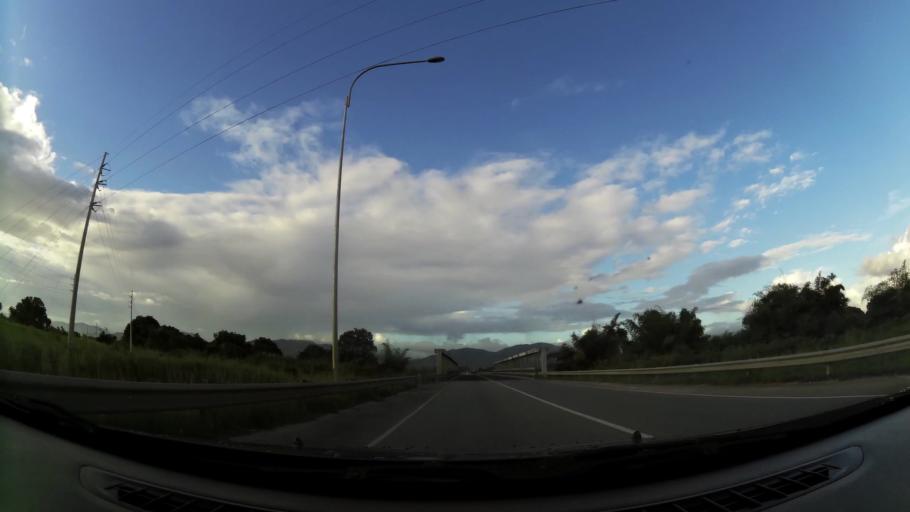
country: TT
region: Tunapuna/Piarco
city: Arouca
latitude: 10.5888
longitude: -61.3555
